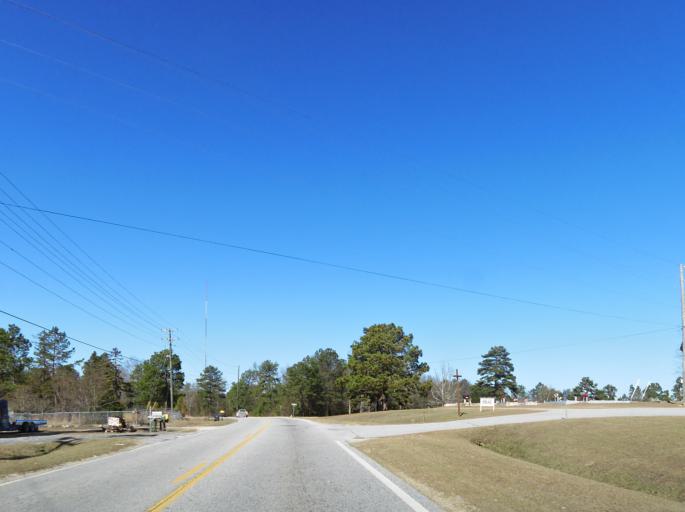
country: US
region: Georgia
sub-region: Bibb County
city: West Point
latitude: 32.7539
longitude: -83.7436
